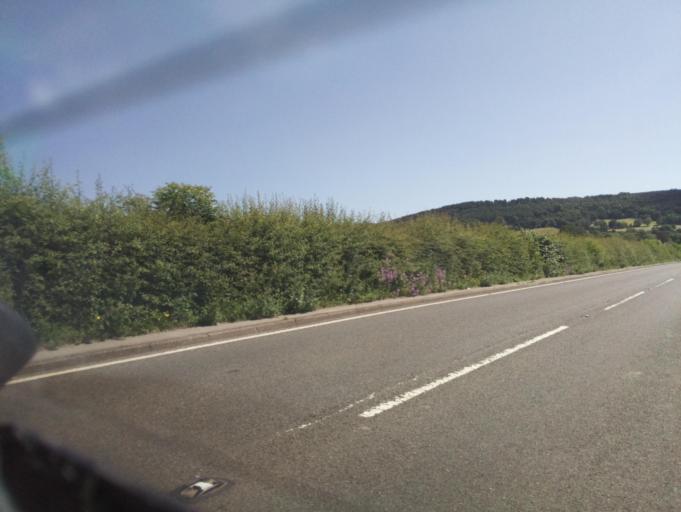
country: GB
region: England
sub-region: Derbyshire
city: Bakewell
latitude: 53.1893
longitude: -1.6261
